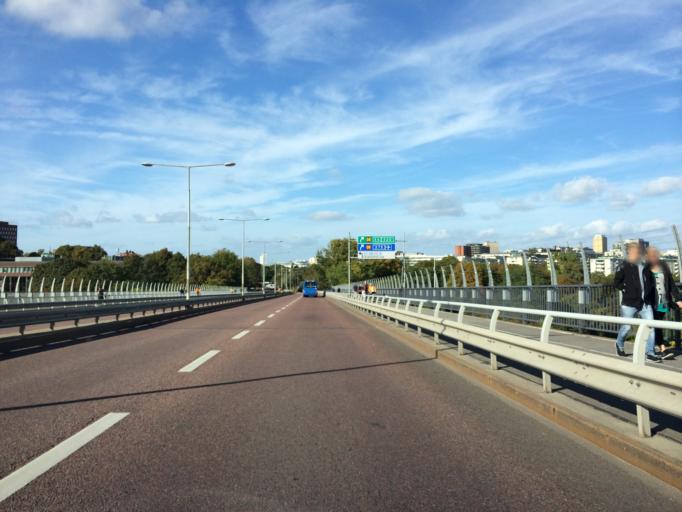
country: SE
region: Stockholm
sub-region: Stockholms Kommun
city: Arsta
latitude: 59.3254
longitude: 18.0261
